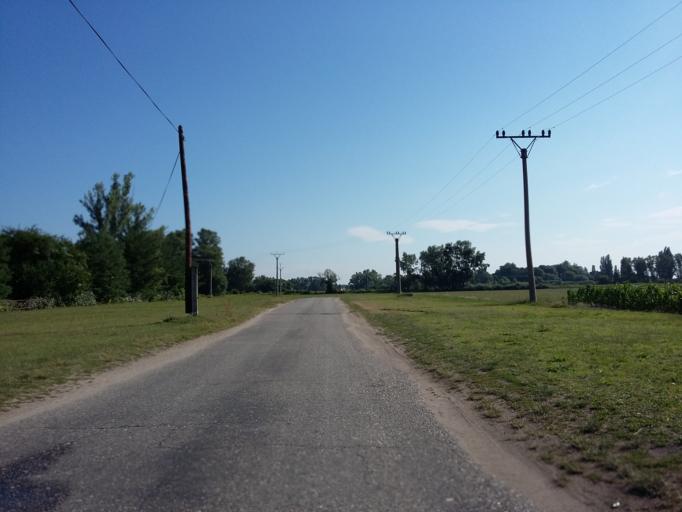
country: AT
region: Lower Austria
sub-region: Politischer Bezirk Ganserndorf
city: Drosing
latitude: 48.4913
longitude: 16.9627
